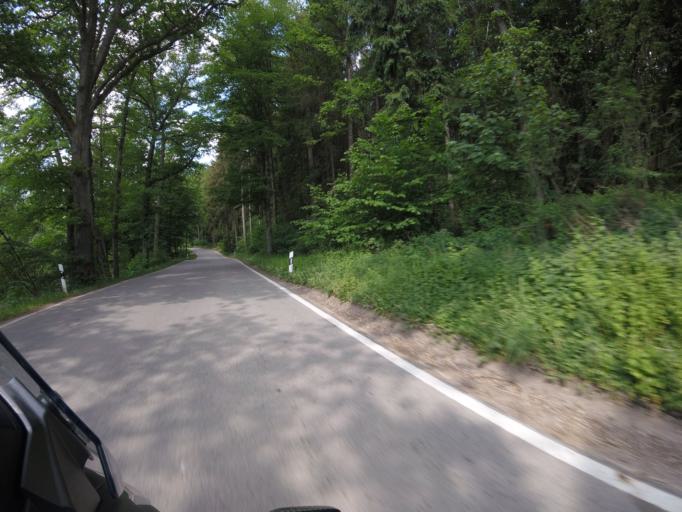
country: DE
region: Bavaria
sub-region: Upper Bavaria
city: Wolfersdorf
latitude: 48.4584
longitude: 11.7344
